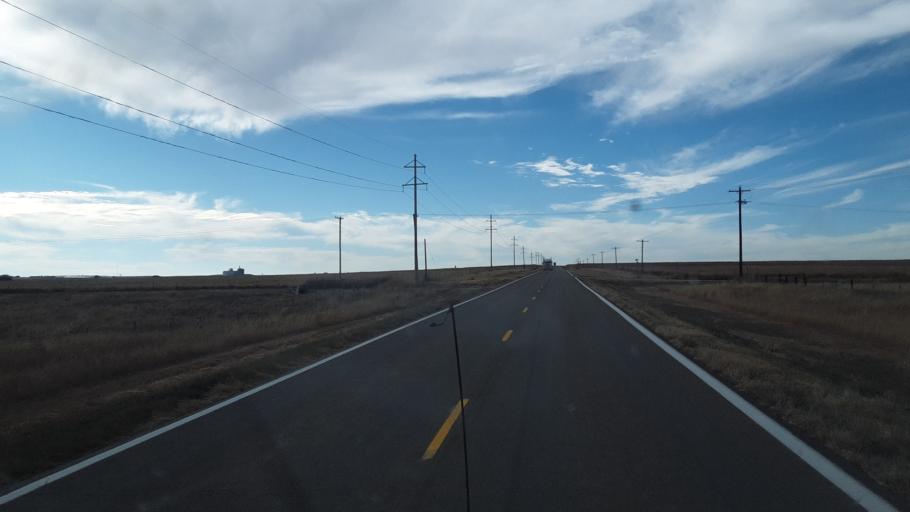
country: US
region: Kansas
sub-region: Hodgeman County
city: Jetmore
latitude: 38.0879
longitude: -99.8611
